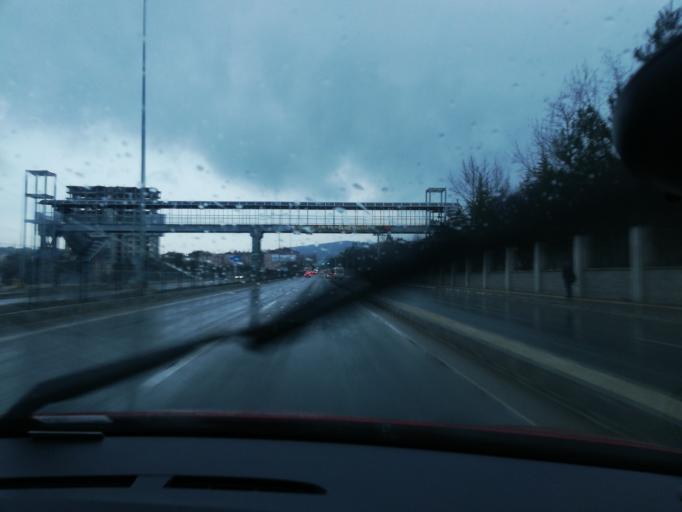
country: TR
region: Kastamonu
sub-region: Cide
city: Kastamonu
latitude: 41.4128
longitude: 33.7933
